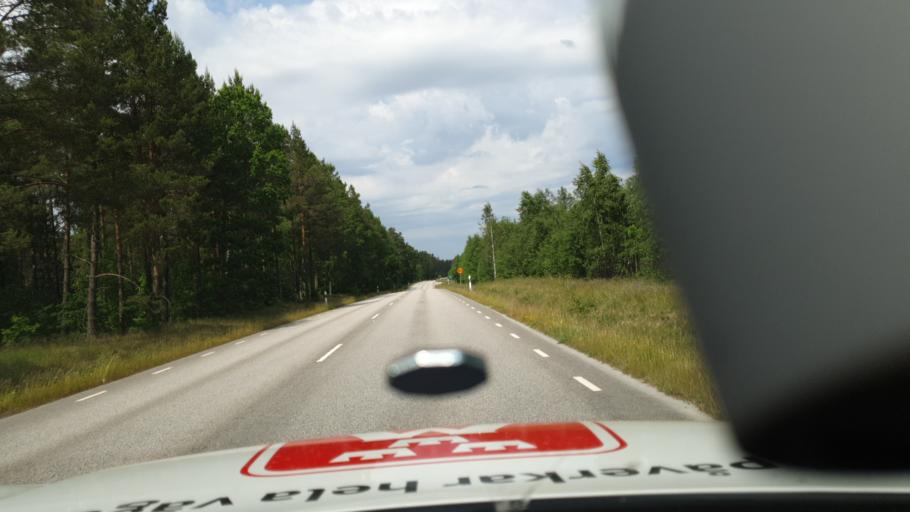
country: SE
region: Joenkoeping
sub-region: Varnamo Kommun
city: Varnamo
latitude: 57.2235
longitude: 14.0411
